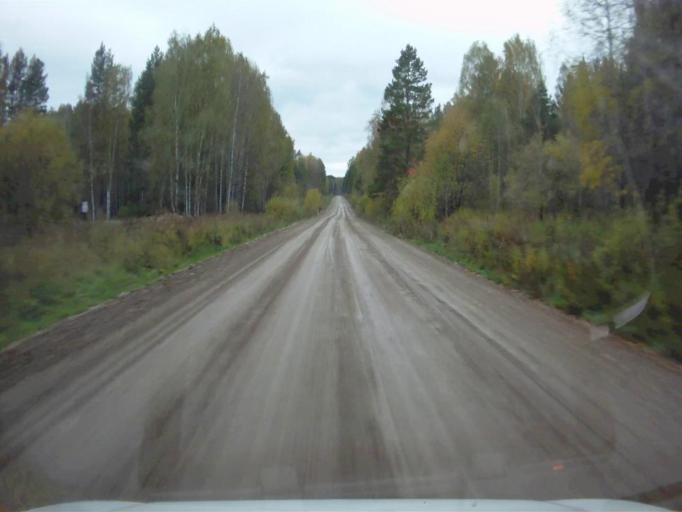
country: RU
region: Chelyabinsk
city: Nyazepetrovsk
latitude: 56.0929
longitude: 59.4086
